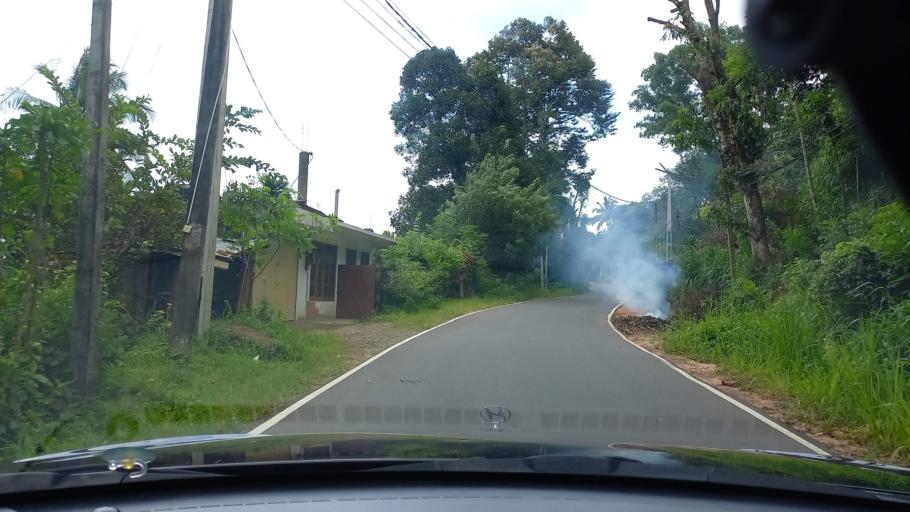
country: LK
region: Central
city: Gampola
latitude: 7.2225
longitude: 80.6072
